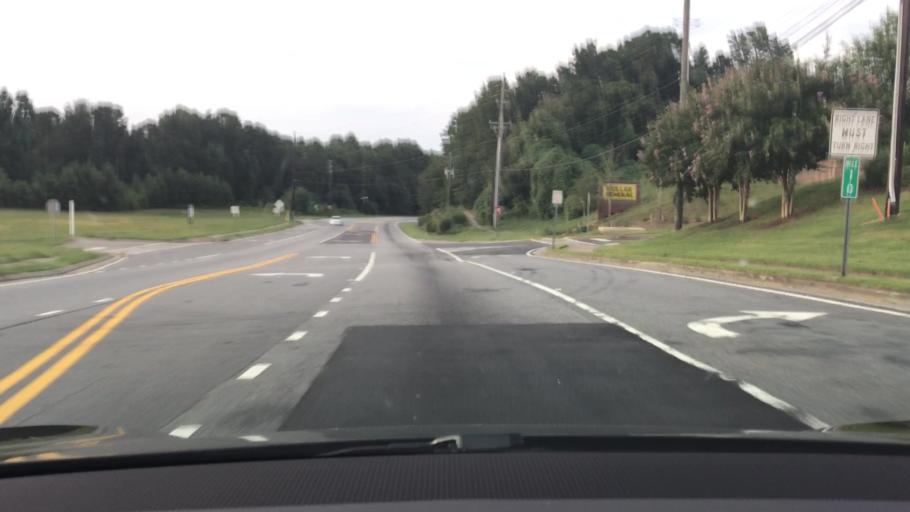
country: US
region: Georgia
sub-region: Gwinnett County
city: Duluth
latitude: 34.0093
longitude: -84.1309
